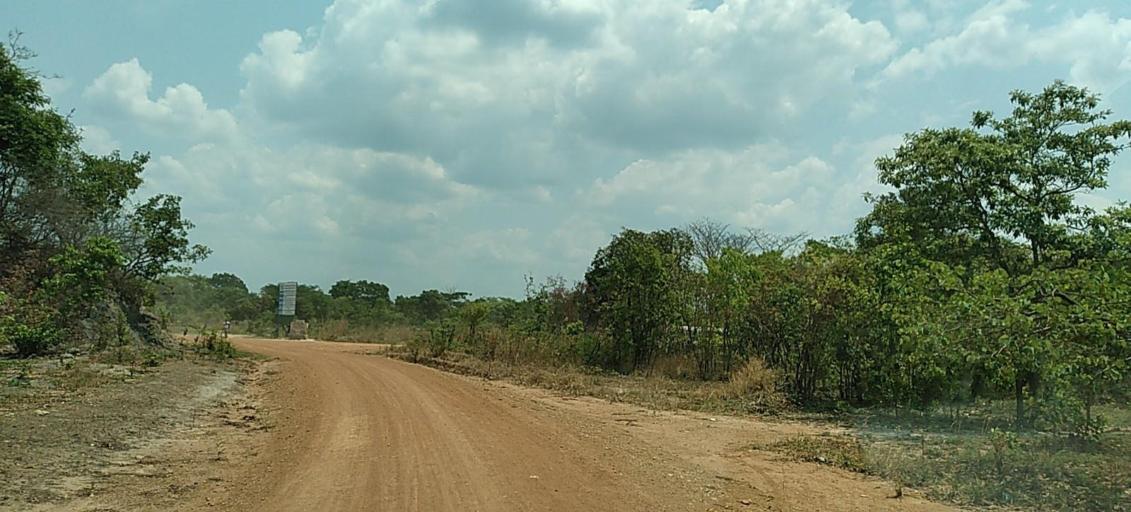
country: ZM
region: Copperbelt
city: Luanshya
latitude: -13.1532
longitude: 28.3143
